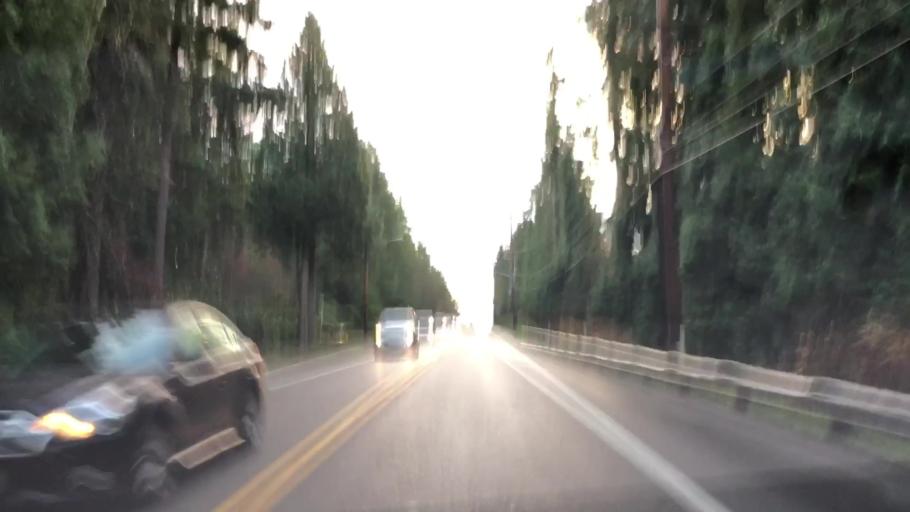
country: US
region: Washington
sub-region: King County
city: Sammamish
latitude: 47.6391
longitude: -122.0511
